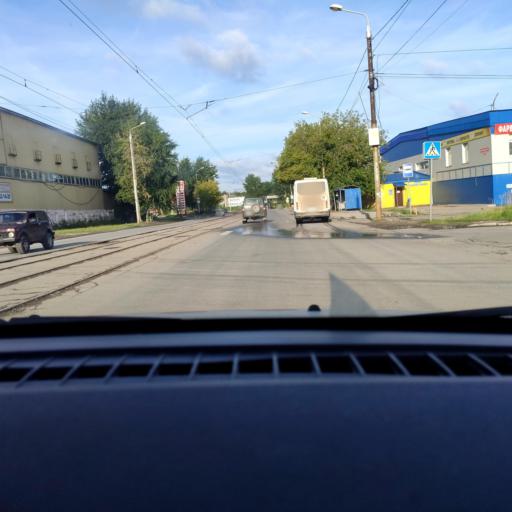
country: RU
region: Perm
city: Kondratovo
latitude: 58.0086
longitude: 56.1753
